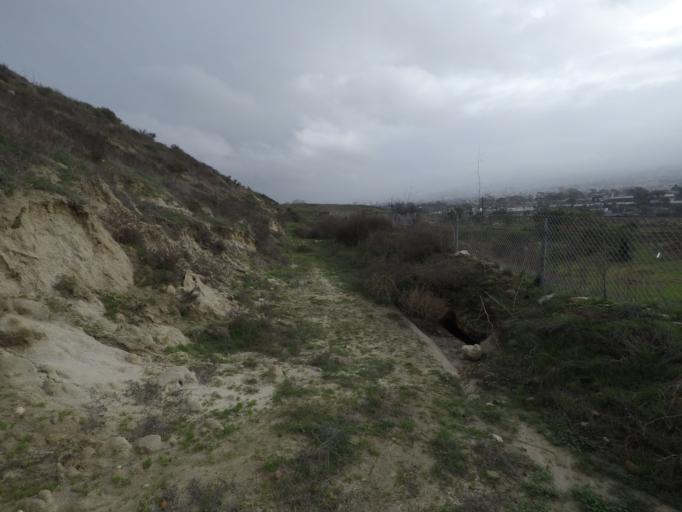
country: MX
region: Baja California
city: Tijuana
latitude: 32.5556
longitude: -117.0386
